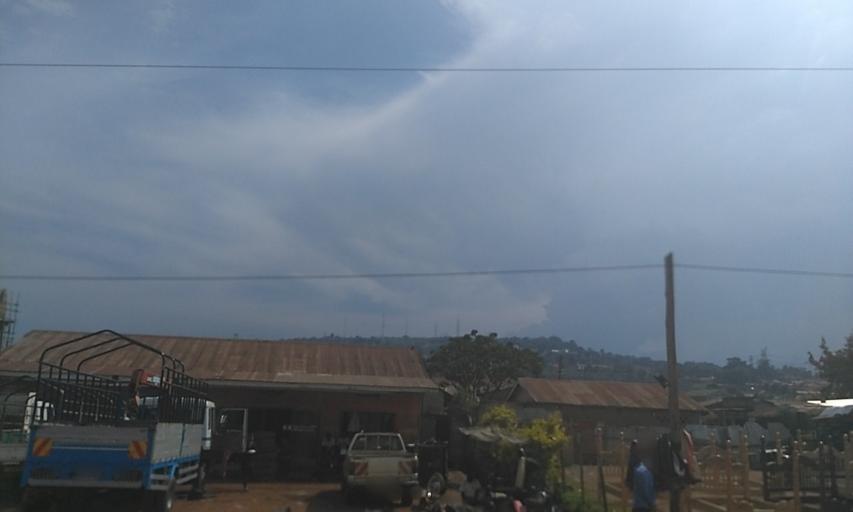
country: UG
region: Central Region
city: Kampala Central Division
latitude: 0.2980
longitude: 32.5366
